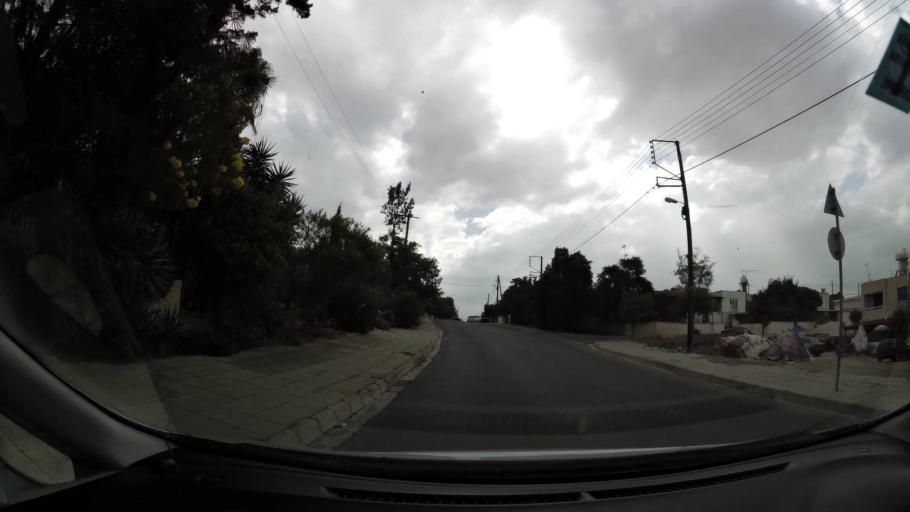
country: CY
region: Lefkosia
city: Geri
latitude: 35.1176
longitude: 33.3843
